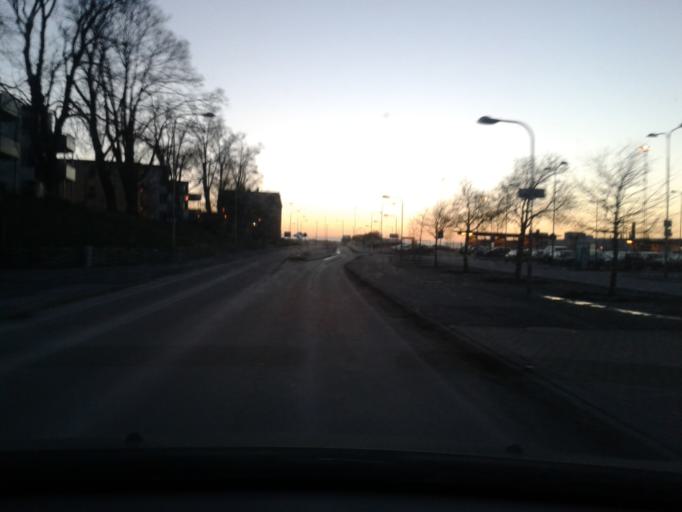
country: SE
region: Gotland
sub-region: Gotland
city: Visby
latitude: 57.6336
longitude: 18.2816
